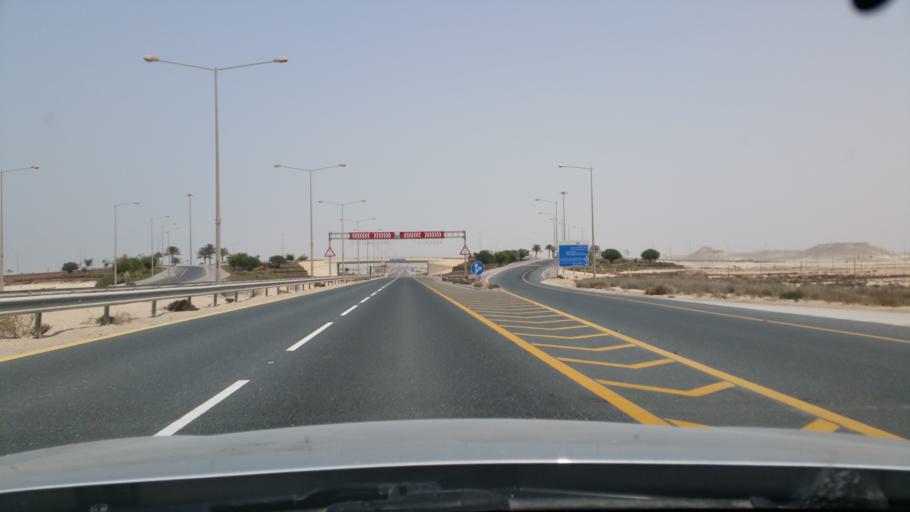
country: QA
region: Baladiyat ar Rayyan
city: Dukhan
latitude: 25.3850
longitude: 50.7822
